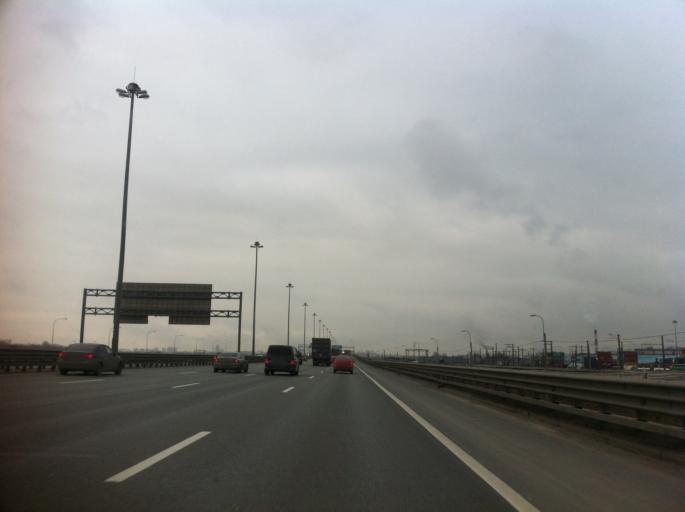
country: RU
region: St.-Petersburg
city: Dachnoye
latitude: 59.8176
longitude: 30.3094
